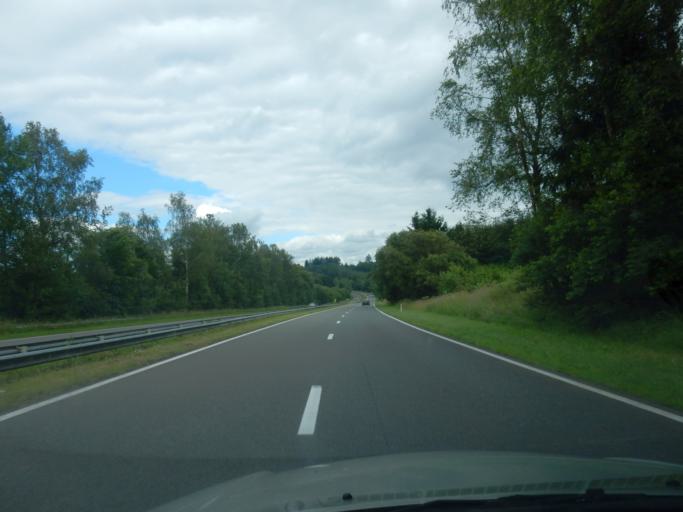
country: BE
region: Wallonia
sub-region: Province du Luxembourg
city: Paliseul
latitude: 49.8608
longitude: 5.1204
